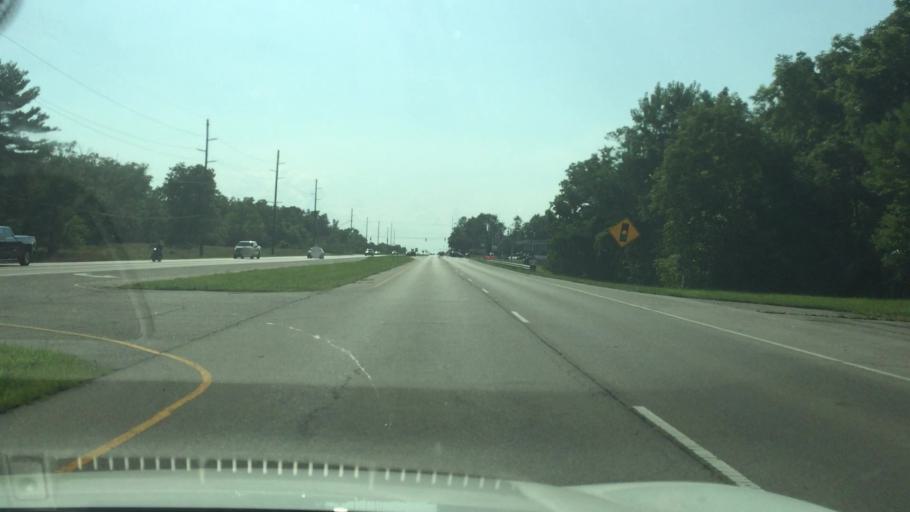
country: US
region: Ohio
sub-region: Clark County
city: Springfield
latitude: 39.9233
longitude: -83.7351
